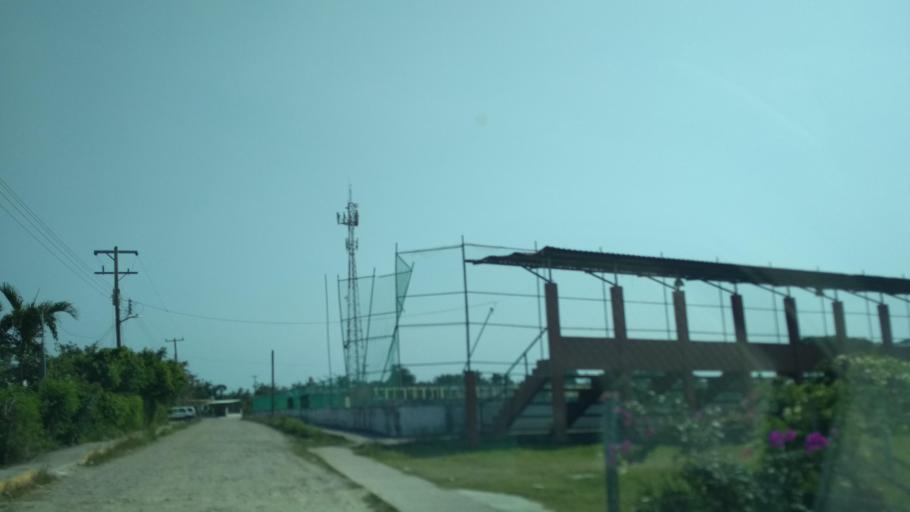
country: MX
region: Veracruz
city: Gutierrez Zamora
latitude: 20.4210
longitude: -97.1884
